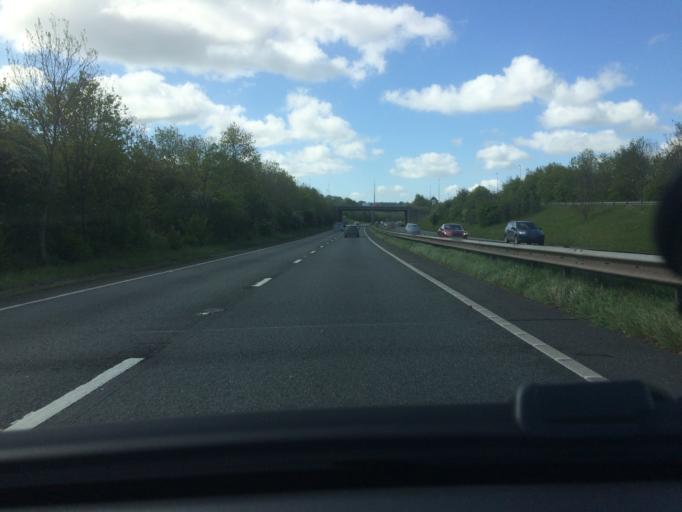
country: GB
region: Wales
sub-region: Wrexham
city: Rossett
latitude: 53.1075
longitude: -2.9560
